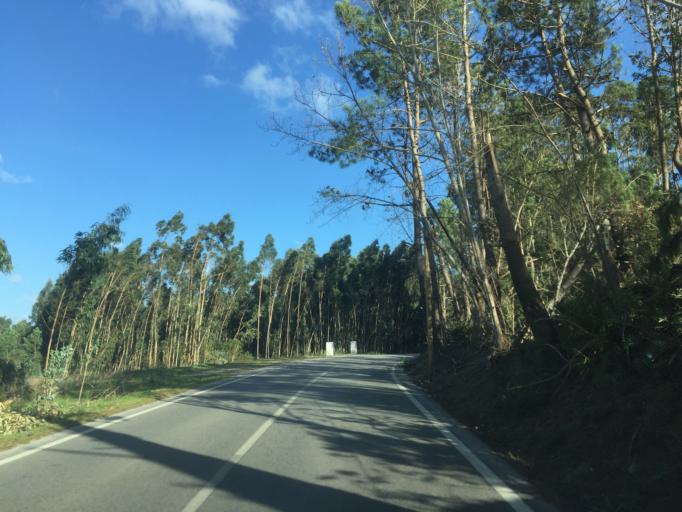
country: PT
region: Coimbra
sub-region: Figueira da Foz
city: Buarcos
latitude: 40.2156
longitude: -8.8733
